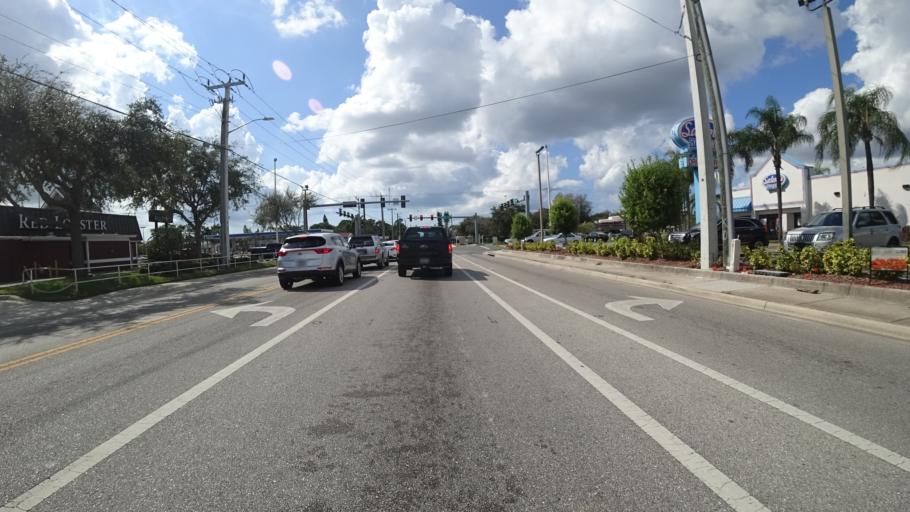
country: US
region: Florida
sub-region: Manatee County
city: Bayshore Gardens
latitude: 27.4404
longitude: -82.5748
